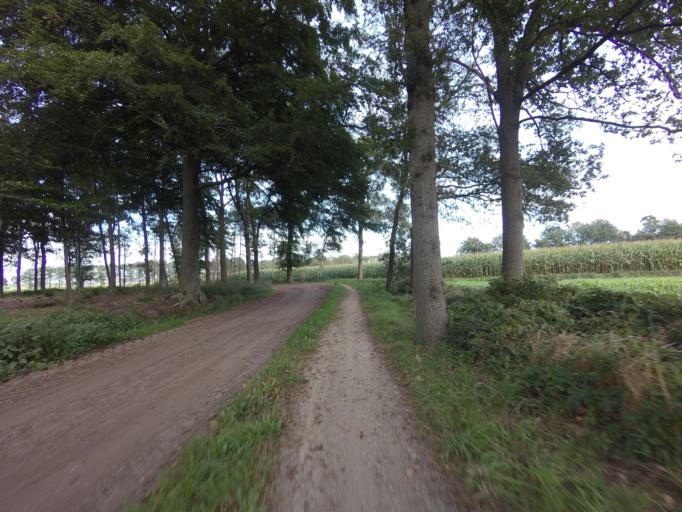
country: NL
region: Overijssel
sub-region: Gemeente Deventer
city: Schalkhaar
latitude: 52.3004
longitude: 6.2399
